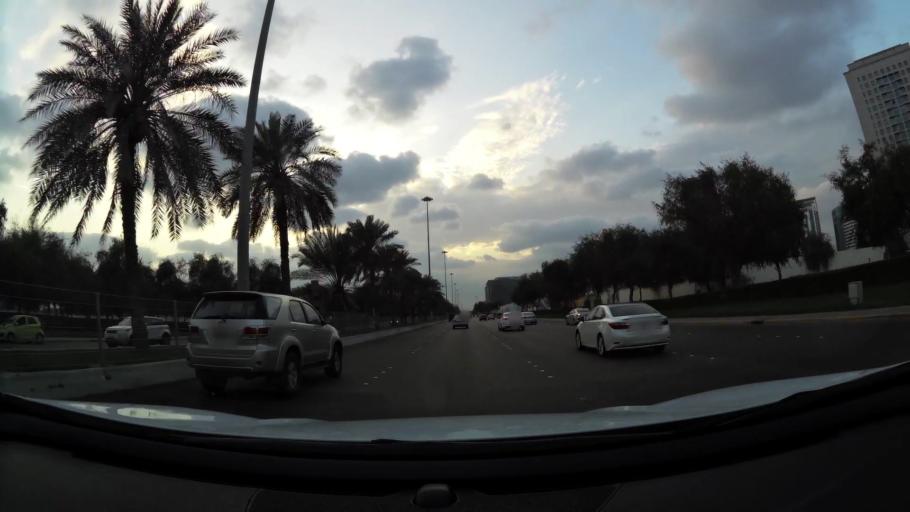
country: AE
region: Abu Dhabi
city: Abu Dhabi
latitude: 24.4276
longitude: 54.4367
